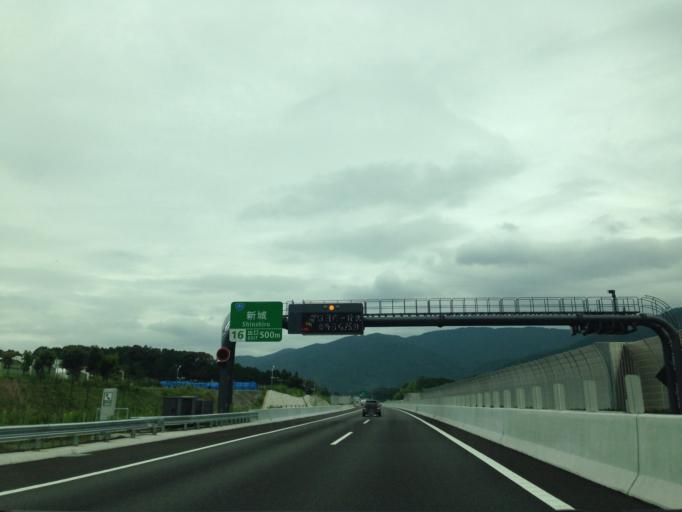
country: JP
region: Aichi
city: Shinshiro
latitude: 34.9242
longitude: 137.5455
